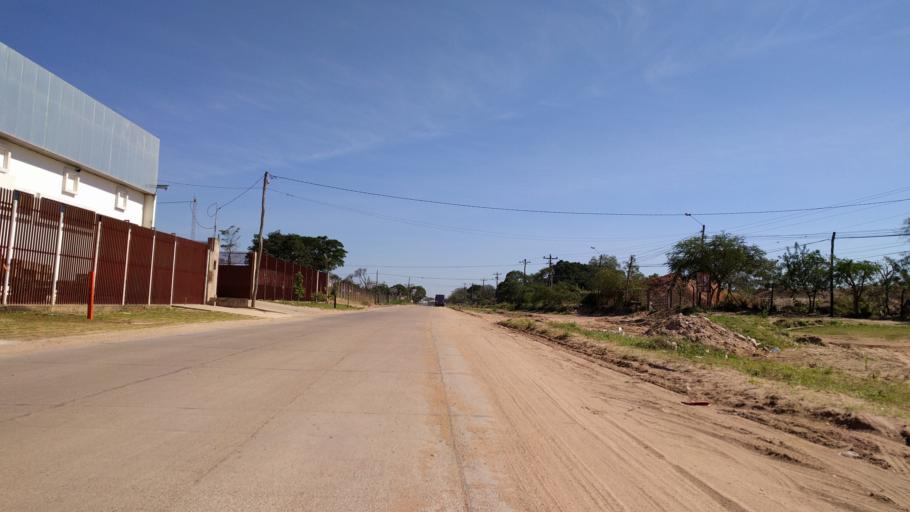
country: BO
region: Santa Cruz
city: Santa Cruz de la Sierra
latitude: -17.8415
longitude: -63.2333
